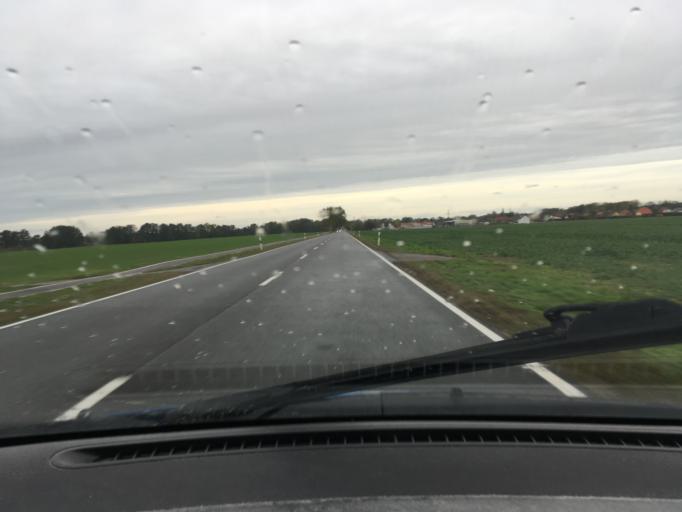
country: DE
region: Saxony-Anhalt
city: Rodleben
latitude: 51.9303
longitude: 12.1433
